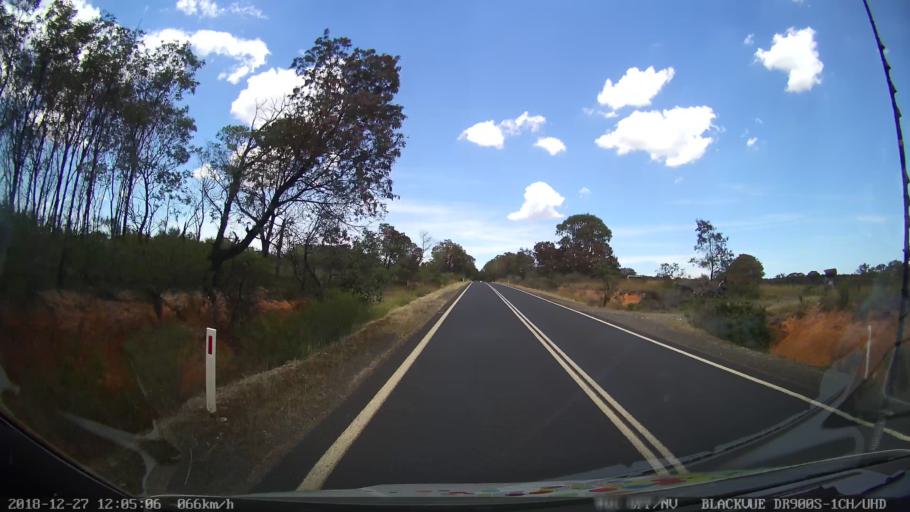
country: AU
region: New South Wales
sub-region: Blayney
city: Blayney
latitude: -33.8003
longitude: 149.3423
